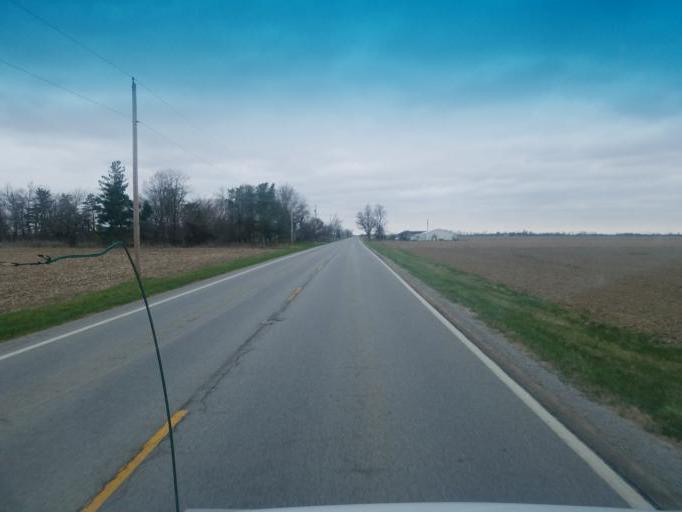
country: US
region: Ohio
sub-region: Allen County
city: Delphos
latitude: 40.9323
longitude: -84.4142
